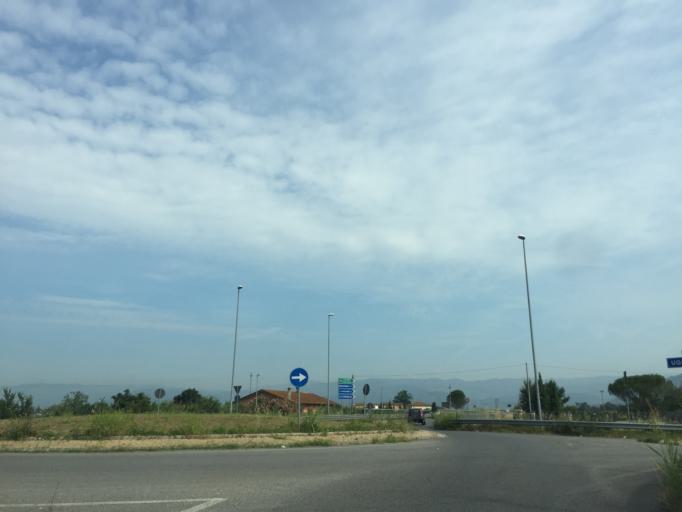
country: IT
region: Tuscany
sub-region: Provincia di Pistoia
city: Uggia-Pazzera-Bizzarrino
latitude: 43.8308
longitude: 10.8286
